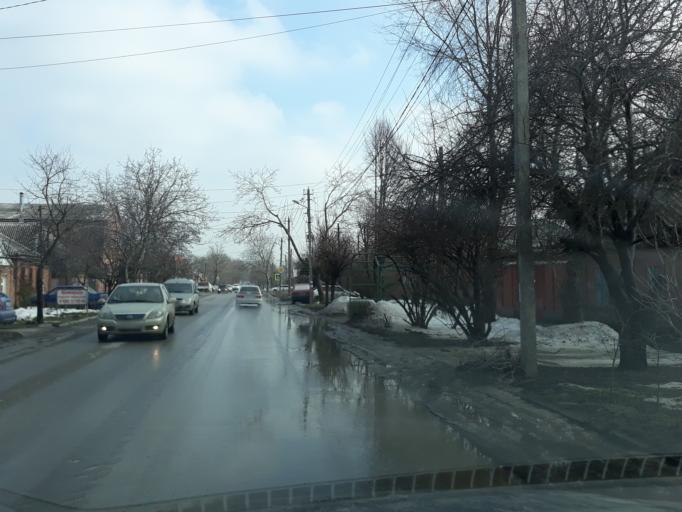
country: RU
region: Rostov
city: Taganrog
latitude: 47.2135
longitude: 38.9054
